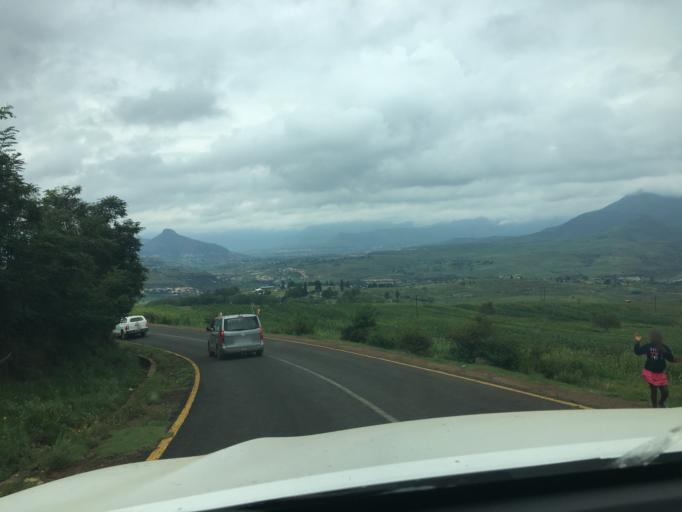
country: LS
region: Berea
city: Teyateyaneng
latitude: -29.2561
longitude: 27.8440
